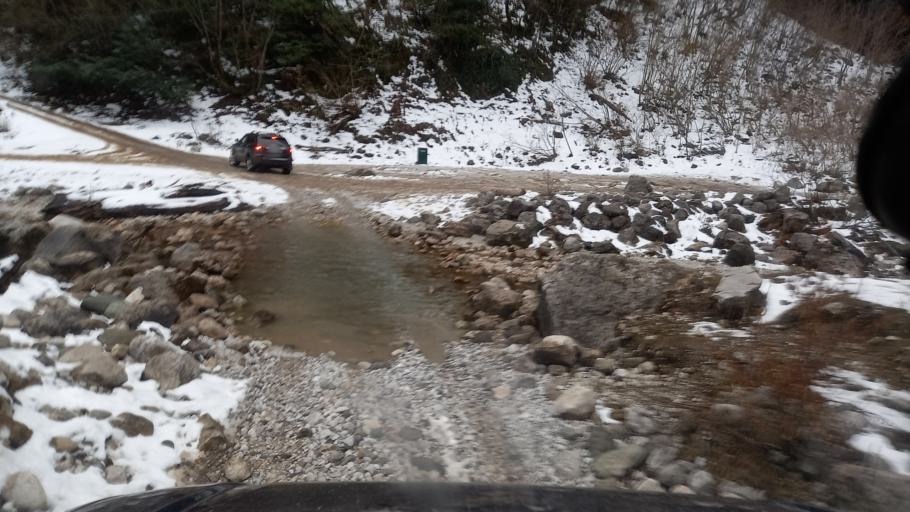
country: GE
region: Abkhazia
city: Gagra
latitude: 43.4352
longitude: 40.4431
